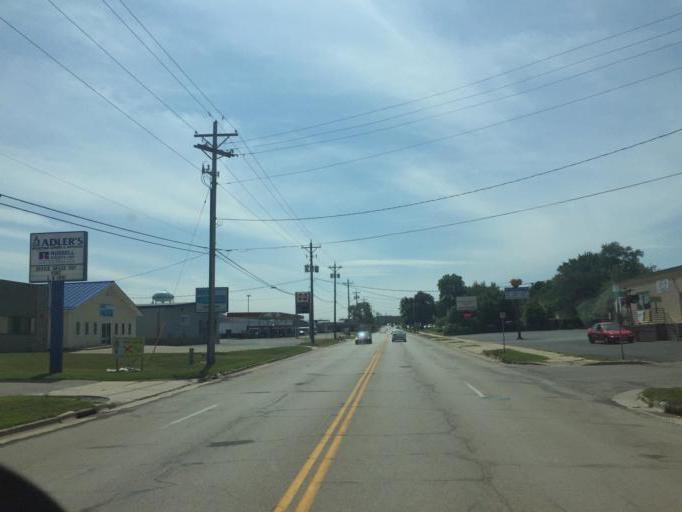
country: US
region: Minnesota
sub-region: Olmsted County
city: Rochester
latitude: 43.9981
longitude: -92.4587
